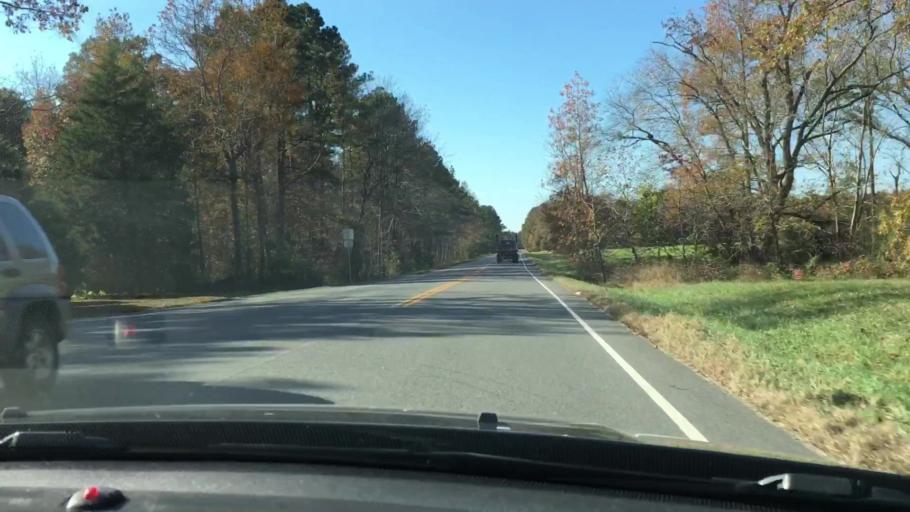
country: US
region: Virginia
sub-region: Hanover County
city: Hanover
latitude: 37.8135
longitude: -77.3019
